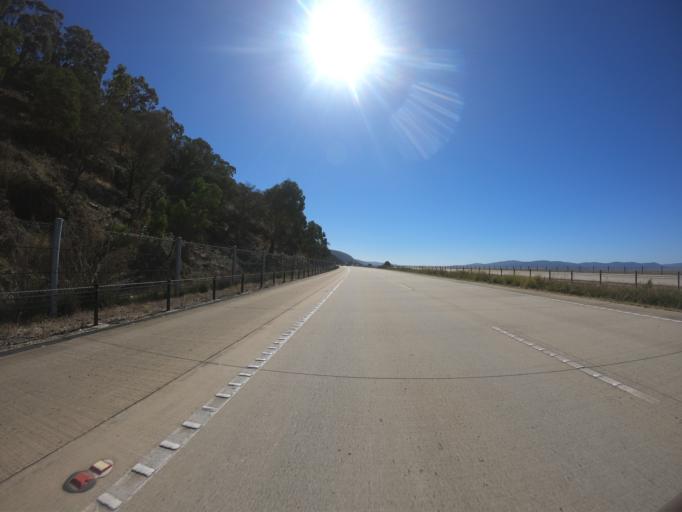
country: AU
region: New South Wales
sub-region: Yass Valley
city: Gundaroo
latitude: -35.0856
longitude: 149.3746
